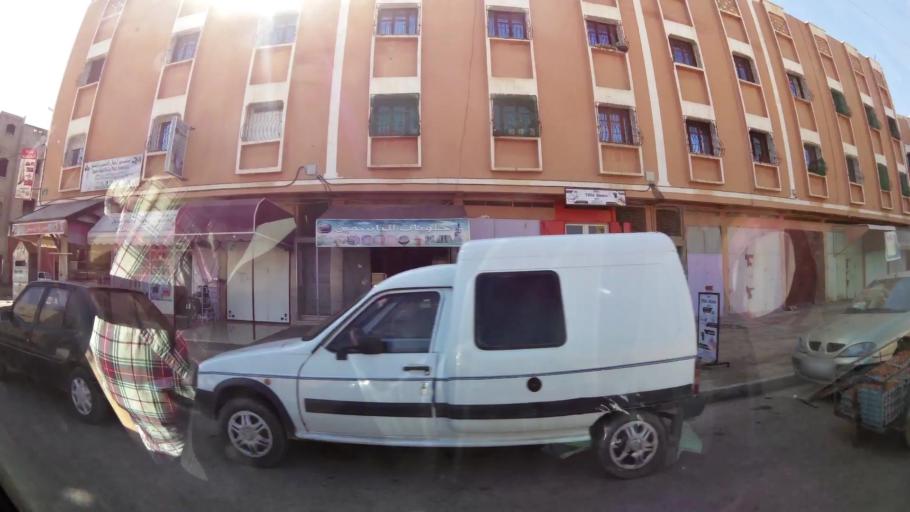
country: MA
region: Souss-Massa-Draa
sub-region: Inezgane-Ait Mellou
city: Inezgane
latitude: 30.3269
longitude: -9.5249
